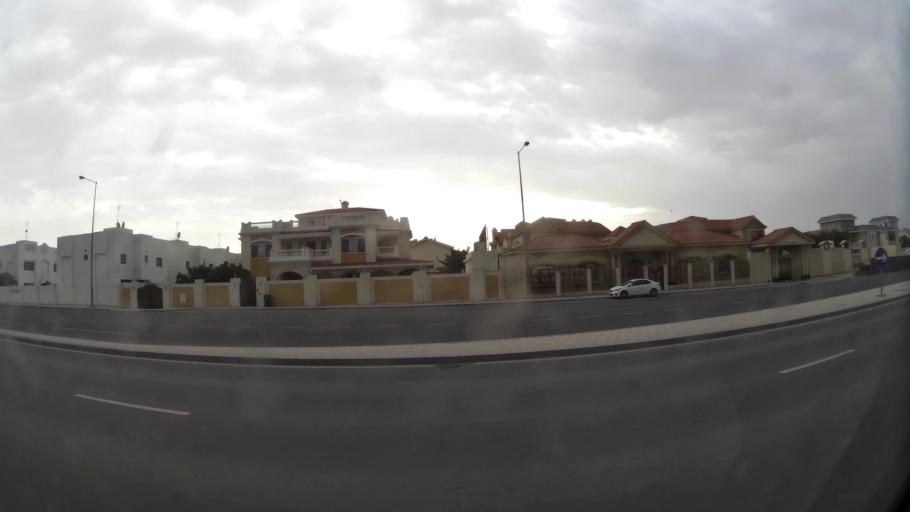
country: QA
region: Baladiyat ad Dawhah
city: Doha
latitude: 25.2586
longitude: 51.4837
